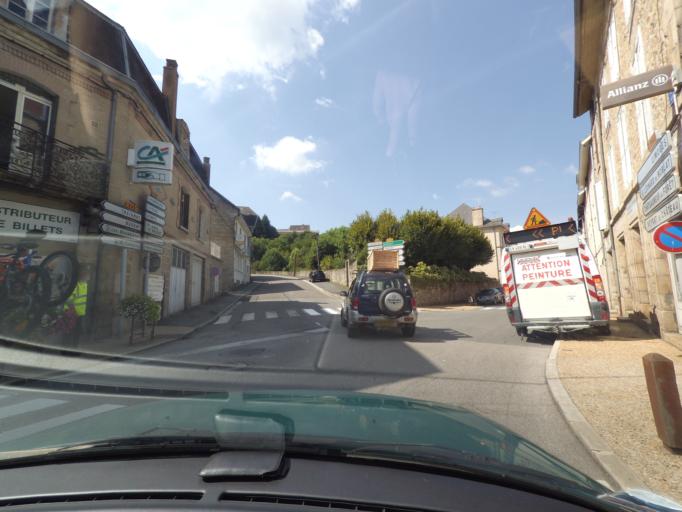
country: FR
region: Limousin
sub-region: Departement de la Haute-Vienne
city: Eymoutiers
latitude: 45.7387
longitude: 1.7411
